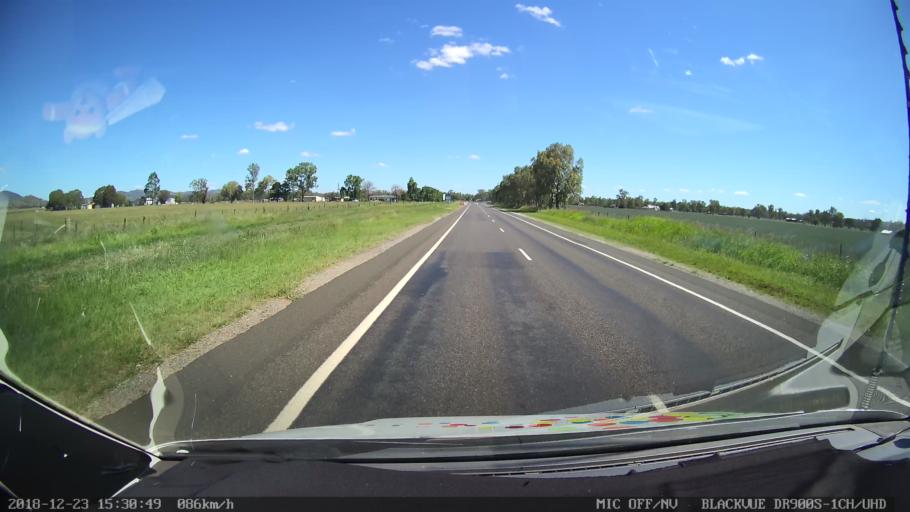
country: AU
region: New South Wales
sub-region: Tamworth Municipality
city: East Tamworth
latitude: -30.9639
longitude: 150.8663
